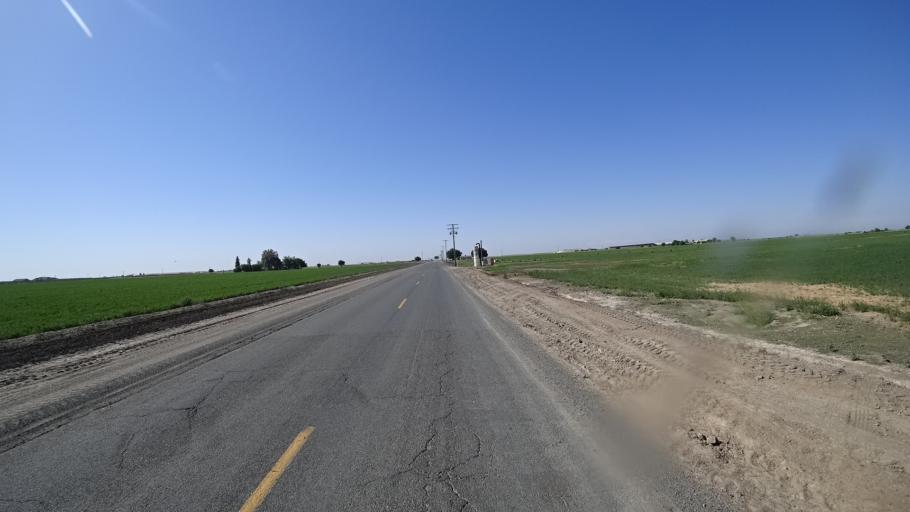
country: US
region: California
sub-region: Kings County
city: Home Garden
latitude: 36.2317
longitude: -119.5472
